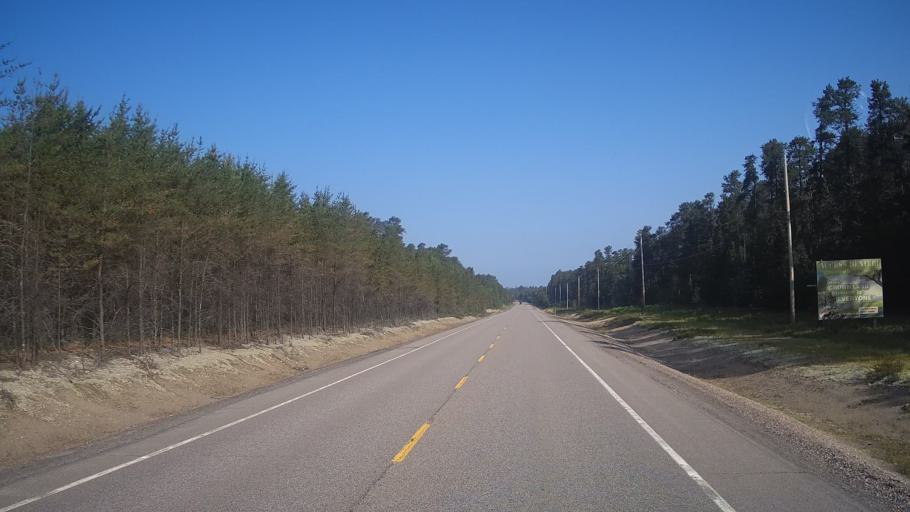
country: CA
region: Ontario
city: Rayside-Balfour
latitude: 46.7232
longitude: -81.5726
